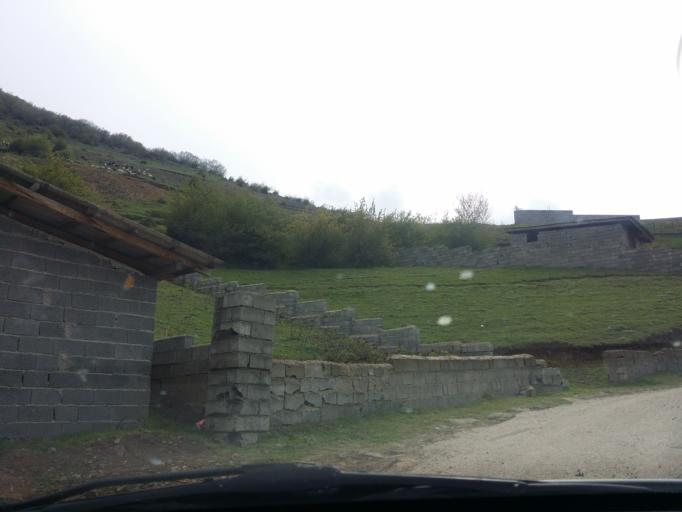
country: IR
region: Mazandaran
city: `Abbasabad
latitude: 36.4851
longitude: 51.1479
